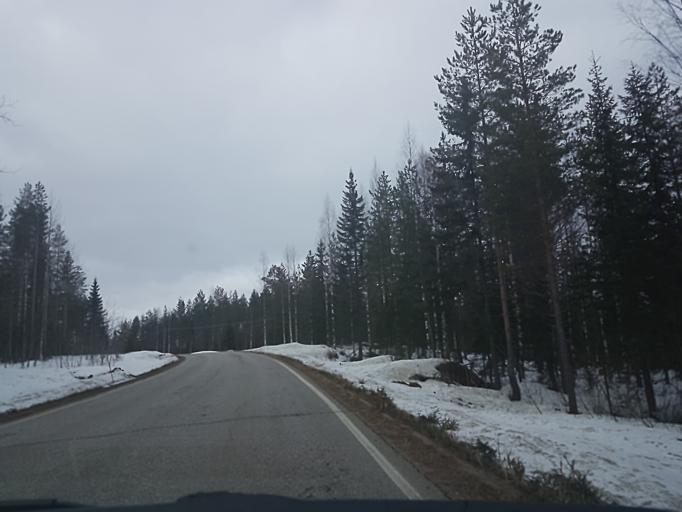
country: FI
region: Northern Savo
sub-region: Koillis-Savo
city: Kaavi
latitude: 63.0396
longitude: 28.5979
